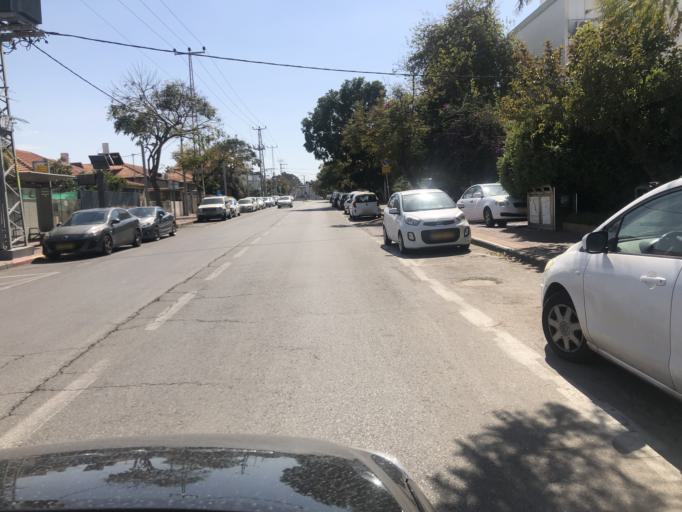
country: IL
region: Tel Aviv
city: Holon
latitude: 32.0090
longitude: 34.7648
